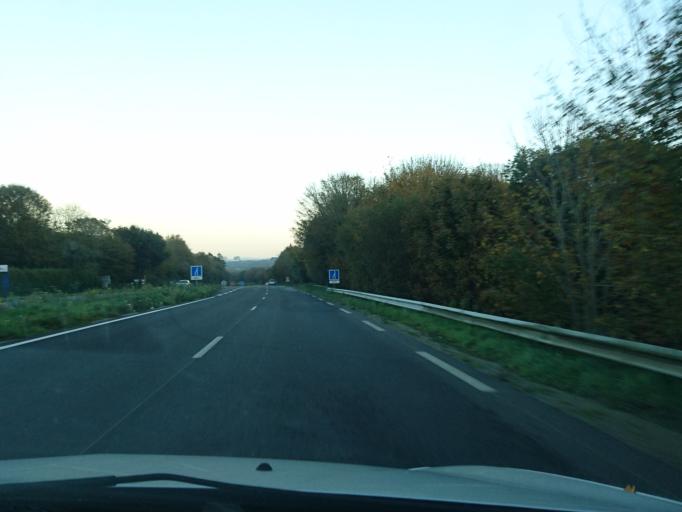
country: FR
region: Brittany
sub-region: Departement du Finistere
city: Guilers
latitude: 48.4135
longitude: -4.5420
